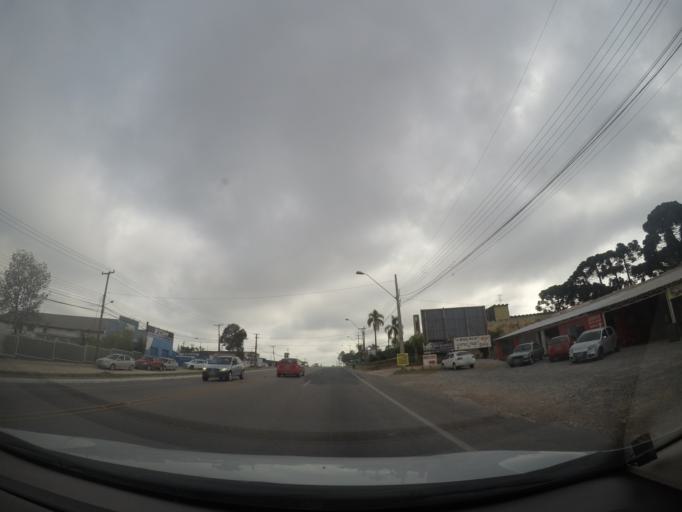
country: BR
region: Parana
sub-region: Colombo
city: Colombo
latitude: -25.3575
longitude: -49.2193
